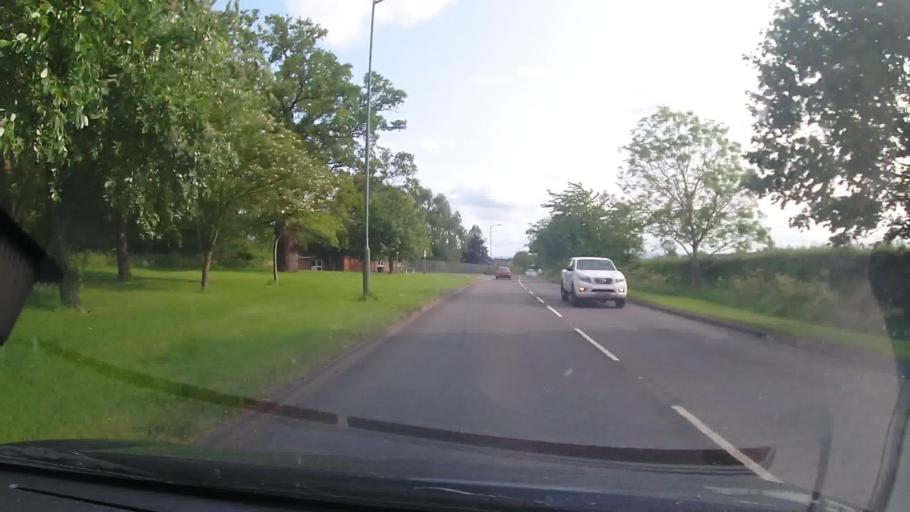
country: GB
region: England
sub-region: Shropshire
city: Shrewsbury
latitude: 52.7383
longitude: -2.7457
